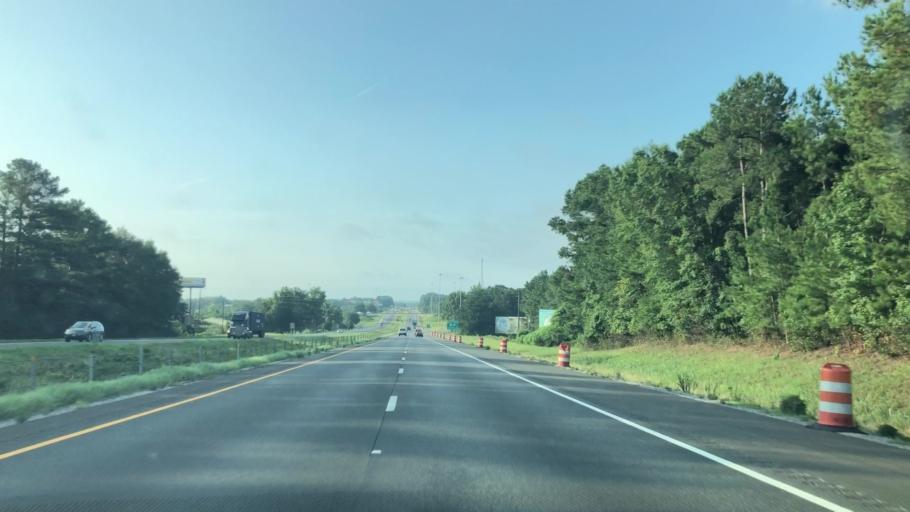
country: US
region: Alabama
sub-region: Chilton County
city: Clanton
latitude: 32.8091
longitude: -86.5831
